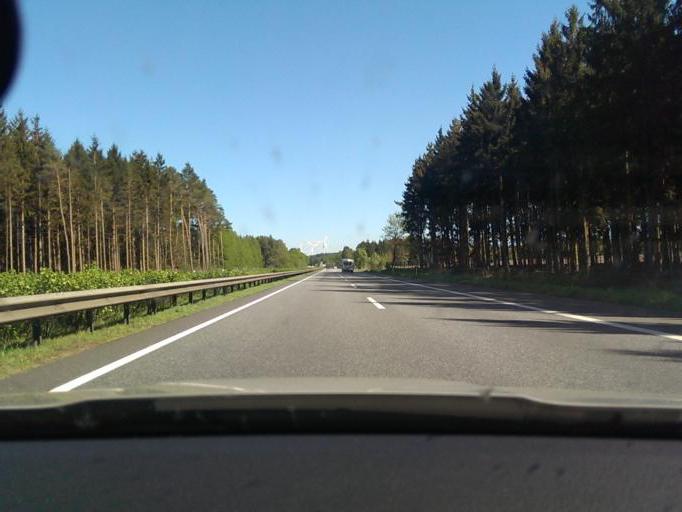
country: DE
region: Lower Saxony
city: Hauslingen
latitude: 52.8956
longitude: 9.4274
